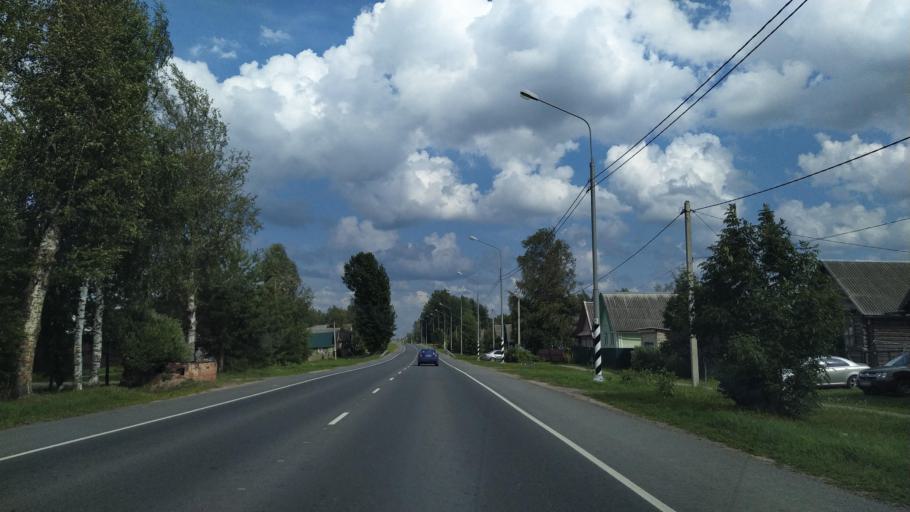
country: RU
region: Novgorod
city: Sol'tsy
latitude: 58.0822
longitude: 30.1045
